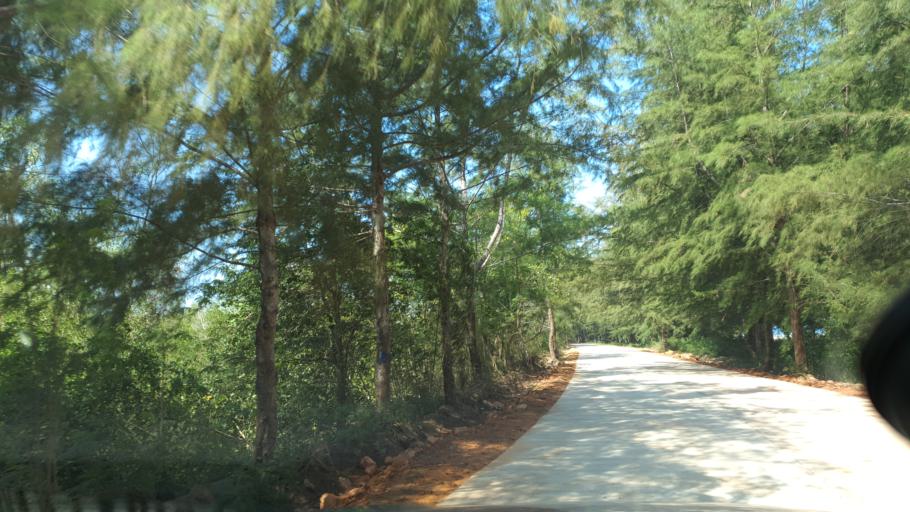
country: TH
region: Surat Thani
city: Tha Chana
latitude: 9.5968
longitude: 99.2093
